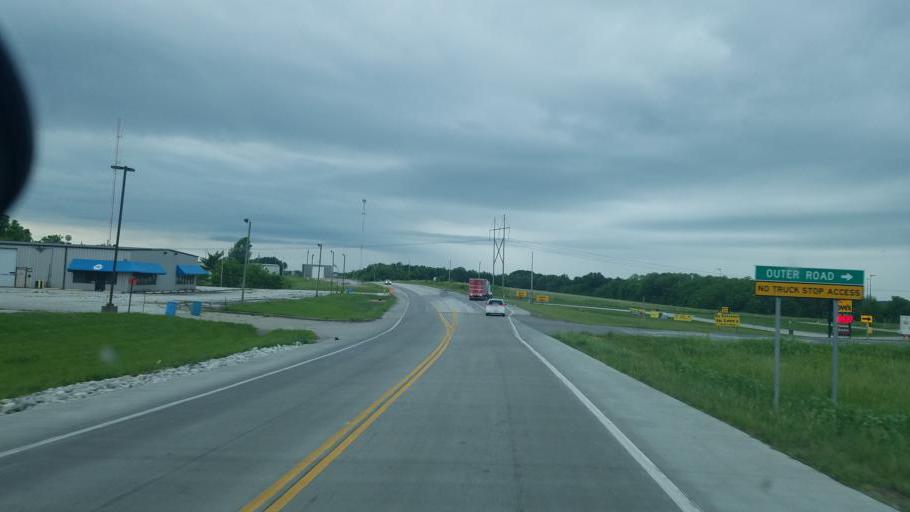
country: US
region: Missouri
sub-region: Cooper County
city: Boonville
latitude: 38.9342
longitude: -92.7777
